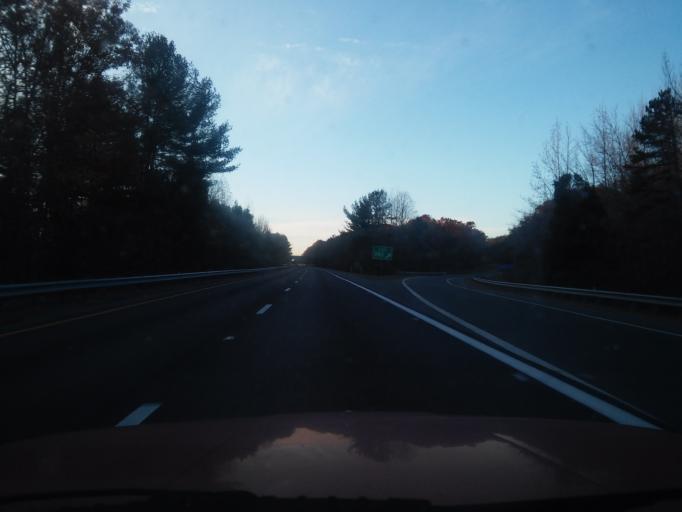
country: US
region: Virginia
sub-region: Louisa County
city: Louisa
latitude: 37.9383
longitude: -78.1038
